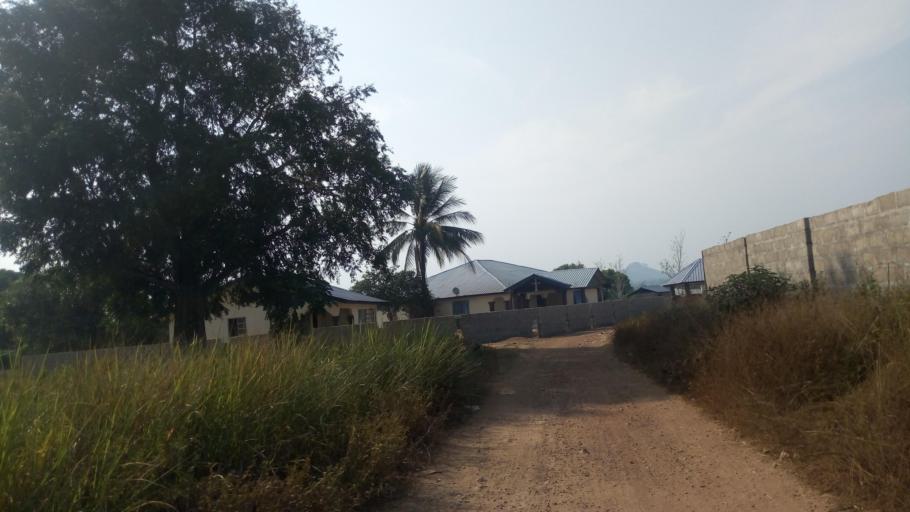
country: SL
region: Southern Province
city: Mogbwemo
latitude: 7.6148
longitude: -12.1792
